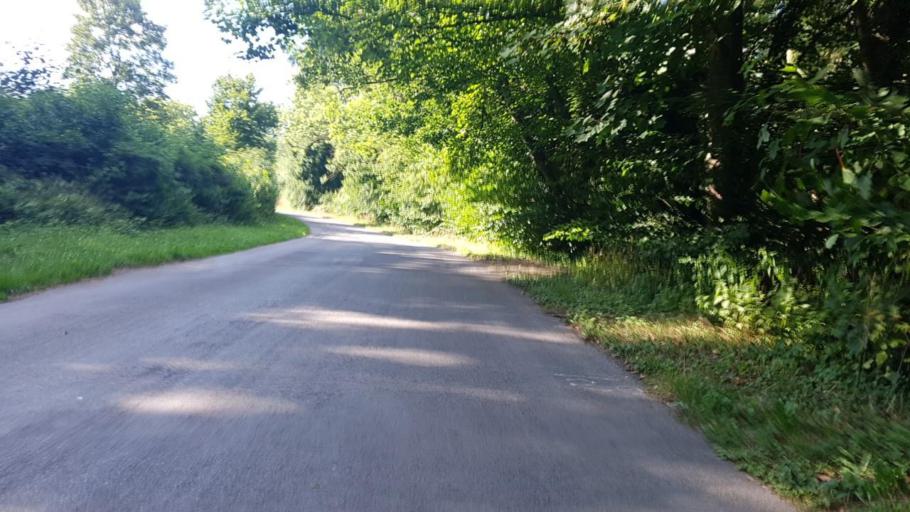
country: FR
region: Picardie
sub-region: Departement de l'Oise
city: Senlis
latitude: 49.1941
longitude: 2.6065
